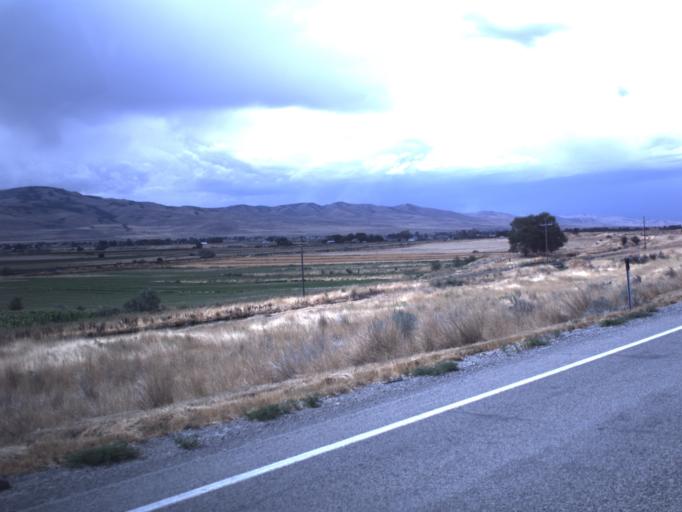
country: US
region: Utah
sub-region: Box Elder County
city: Elwood
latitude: 41.7320
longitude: -112.0983
